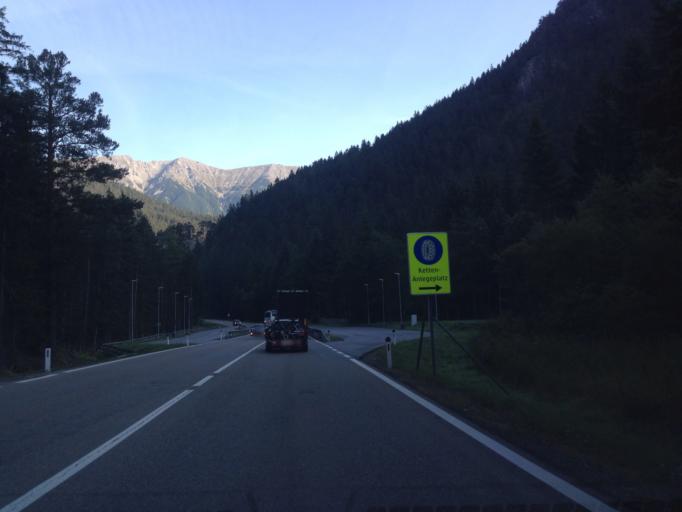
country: AT
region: Tyrol
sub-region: Politischer Bezirk Imst
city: Nassereith
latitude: 47.3340
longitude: 10.8187
